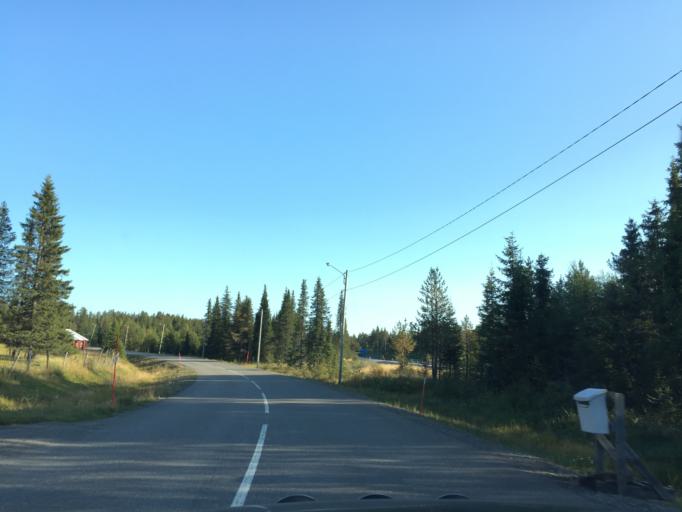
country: SE
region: Norrbotten
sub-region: Gallivare Kommun
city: Malmberget
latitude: 67.6411
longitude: 21.0607
